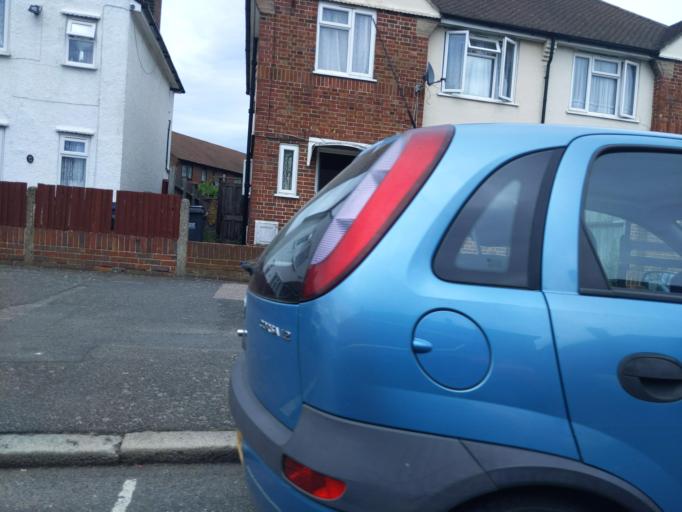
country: GB
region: England
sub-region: Greater London
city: Croydon
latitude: 51.3797
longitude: -0.1096
